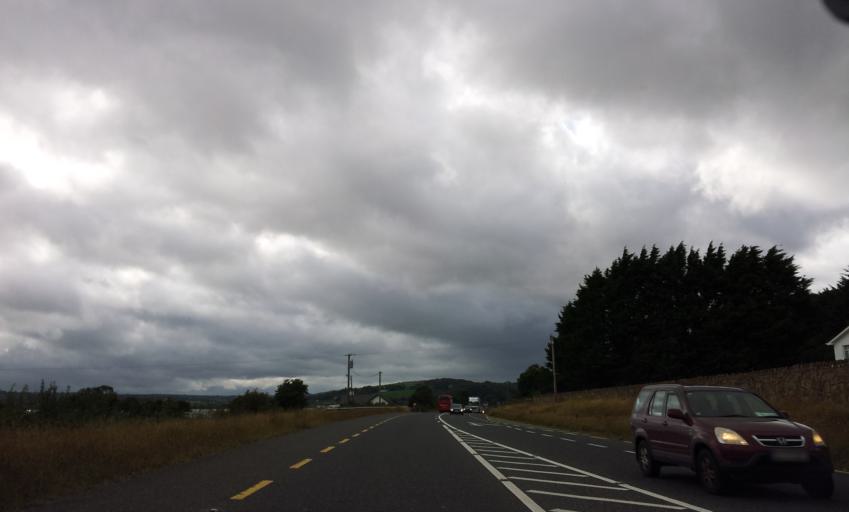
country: IE
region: Munster
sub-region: County Cork
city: Youghal
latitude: 51.9750
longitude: -7.8288
